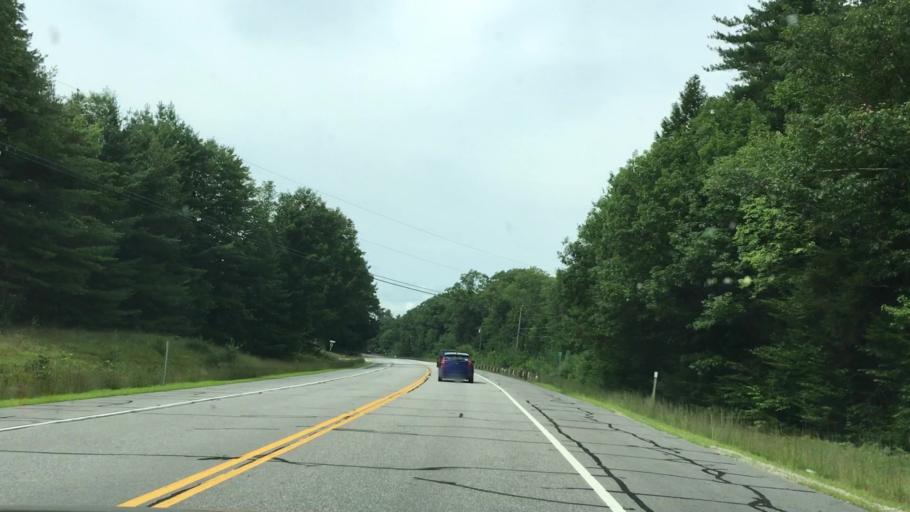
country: US
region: New Hampshire
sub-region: Hillsborough County
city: Antrim
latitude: 43.0666
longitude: -71.9155
